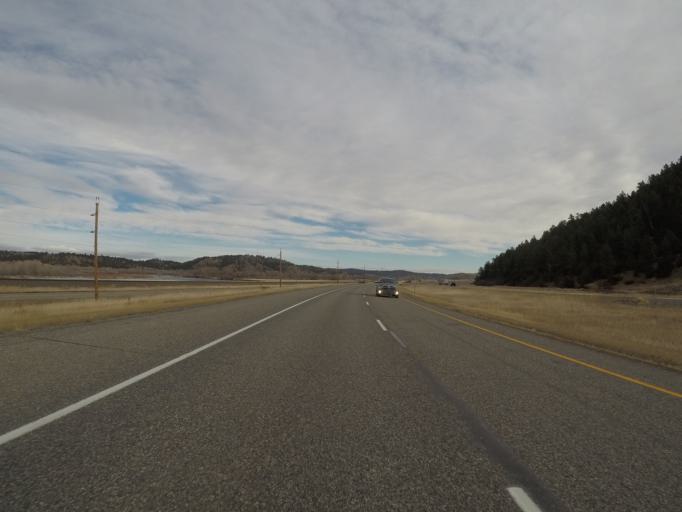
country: US
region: Montana
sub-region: Stillwater County
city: Absarokee
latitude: 45.7110
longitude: -109.5869
